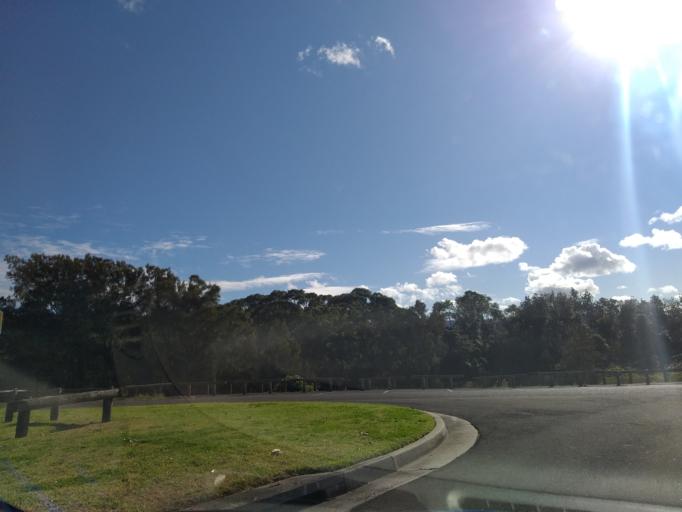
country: AU
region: New South Wales
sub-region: Wollongong
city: East Corrimal
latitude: -34.3645
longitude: 150.9191
